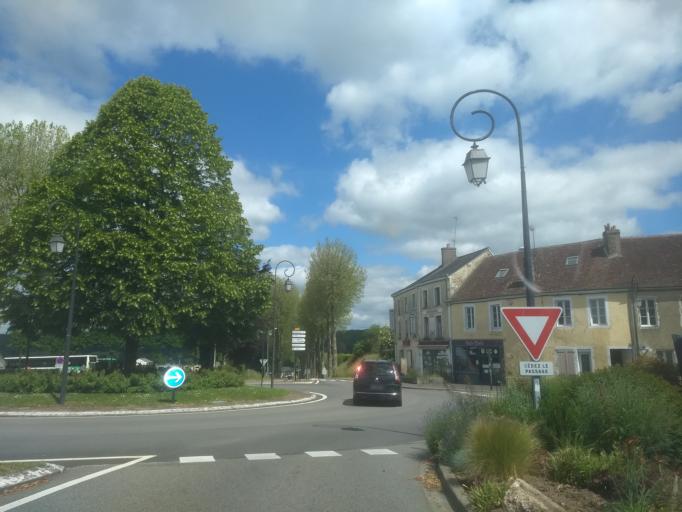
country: FR
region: Lower Normandy
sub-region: Departement de l'Orne
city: Belleme
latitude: 48.3765
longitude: 0.5564
